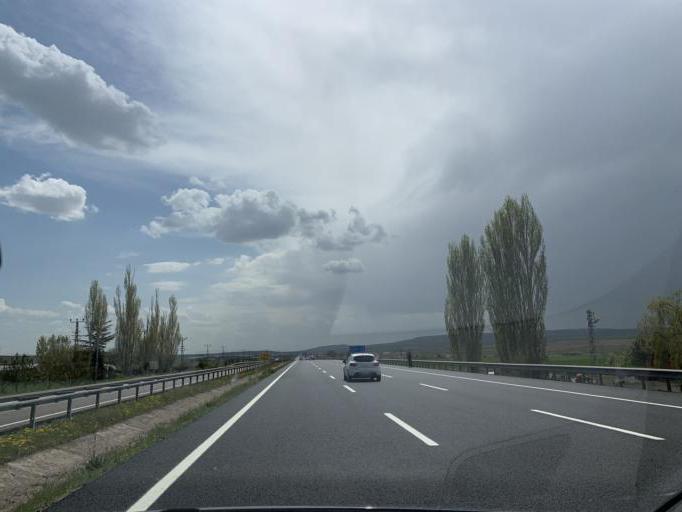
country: TR
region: Ankara
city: Polatli
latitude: 39.6700
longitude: 32.2303
